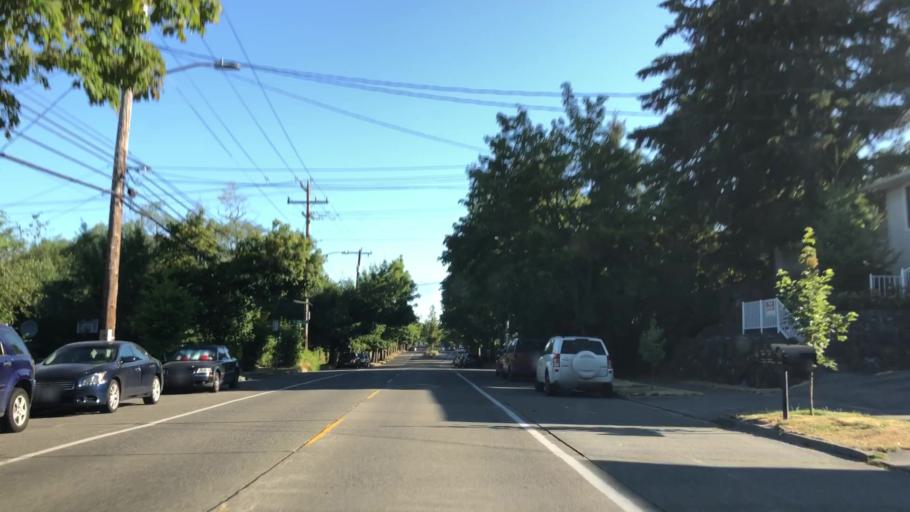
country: US
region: Washington
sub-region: King County
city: White Center
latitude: 47.5424
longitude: -122.3550
